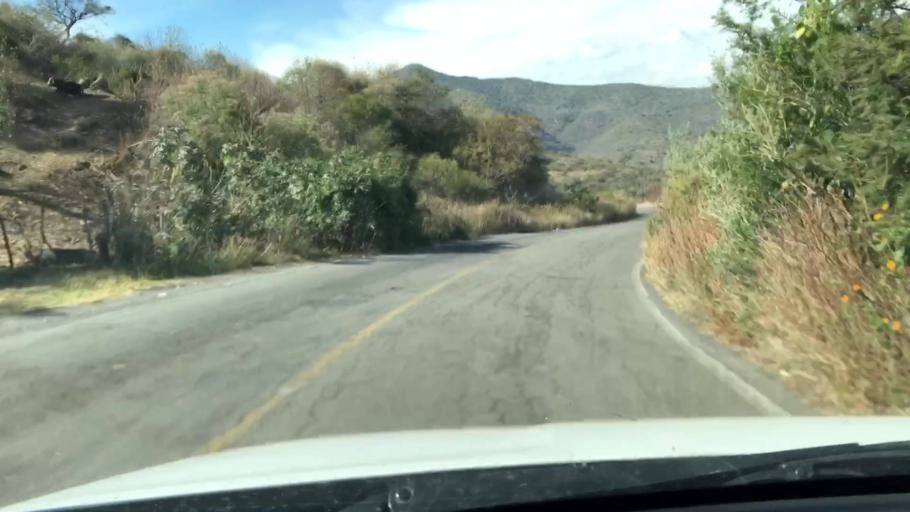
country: MX
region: Jalisco
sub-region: Zacoalco de Torres
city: Barranca de Otates (Barranca de Otatan)
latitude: 20.2505
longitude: -103.6704
